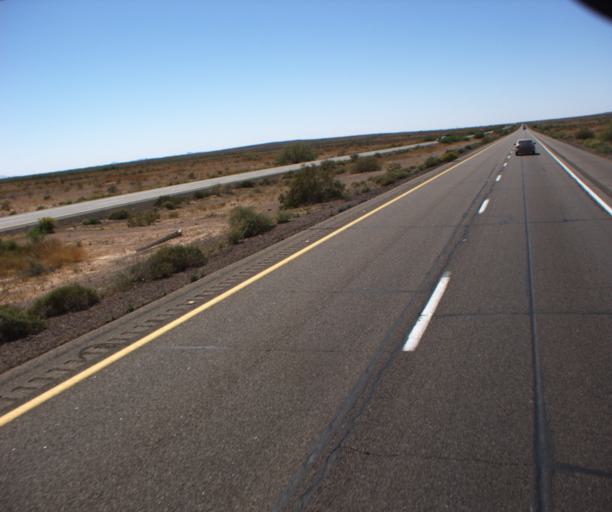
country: US
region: Arizona
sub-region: Maricopa County
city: Gila Bend
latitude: 32.8853
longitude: -113.0869
